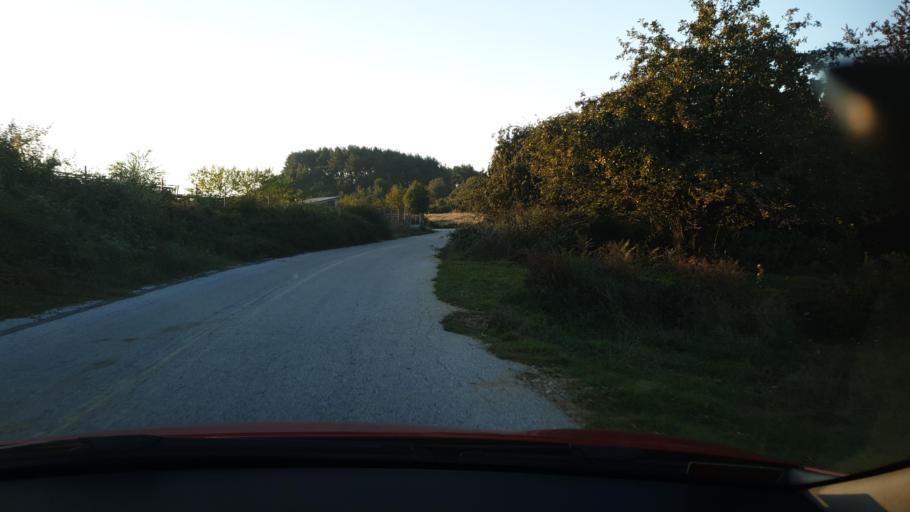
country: GR
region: Central Macedonia
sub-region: Nomos Thessalonikis
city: Peristera
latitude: 40.5082
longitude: 23.2220
